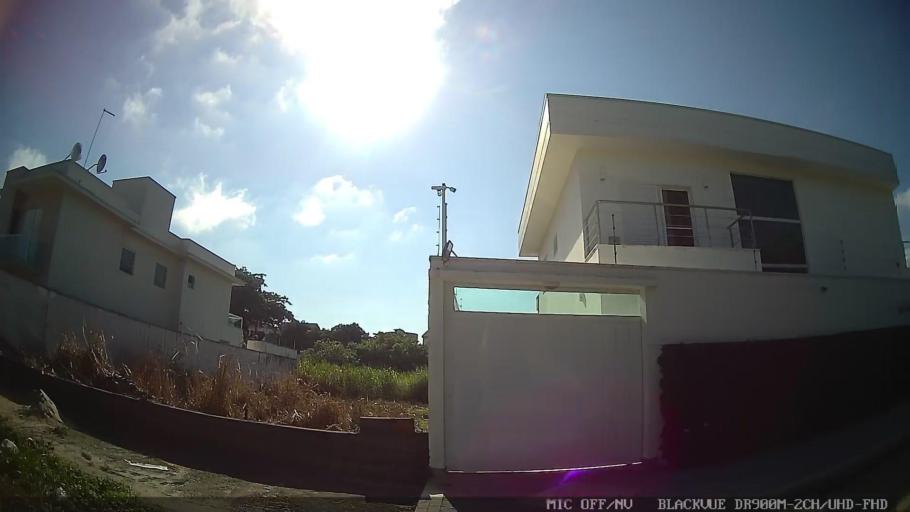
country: BR
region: Sao Paulo
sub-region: Peruibe
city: Peruibe
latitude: -24.2884
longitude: -46.9572
